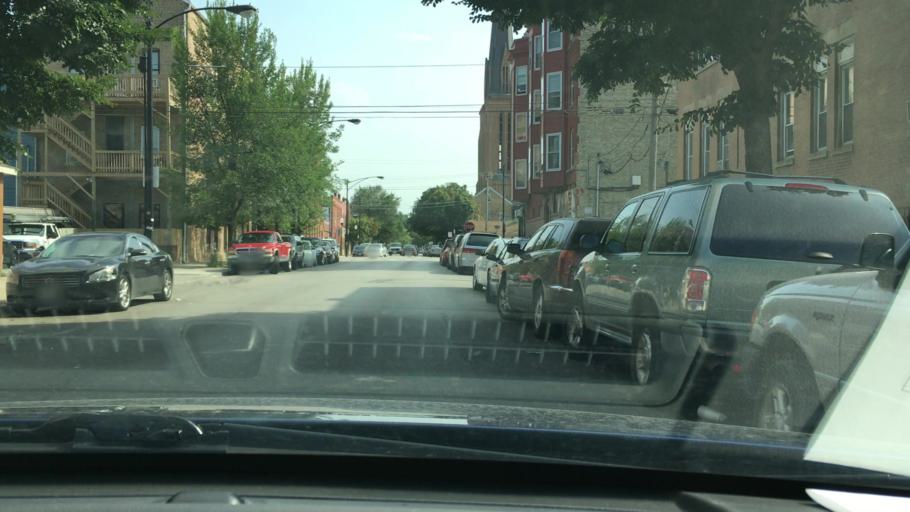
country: US
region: Illinois
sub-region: Cook County
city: Chicago
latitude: 41.8528
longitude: -87.6783
